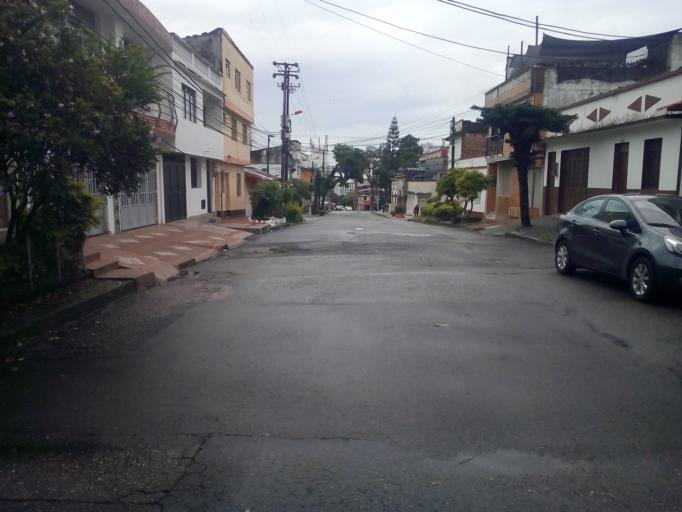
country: CO
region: Tolima
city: Ibague
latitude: 4.4523
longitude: -75.2451
